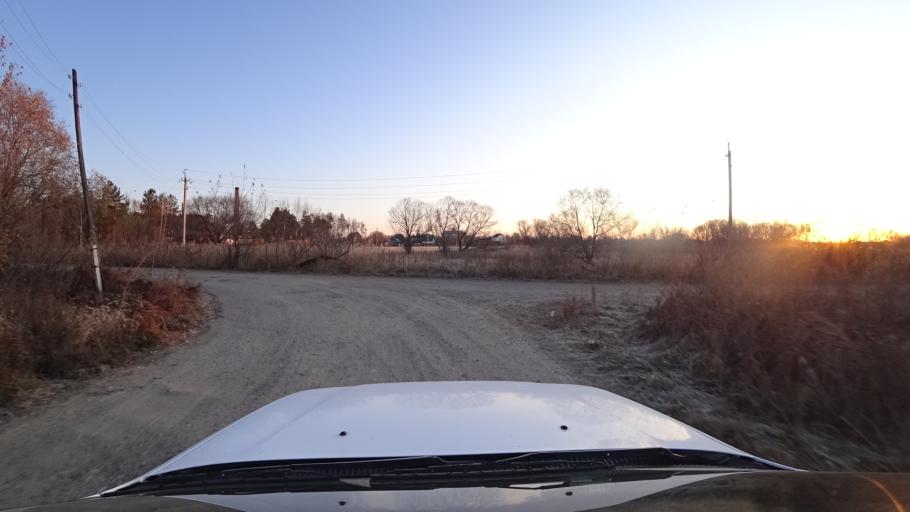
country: RU
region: Primorskiy
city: Dal'nerechensk
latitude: 45.9190
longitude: 133.7373
